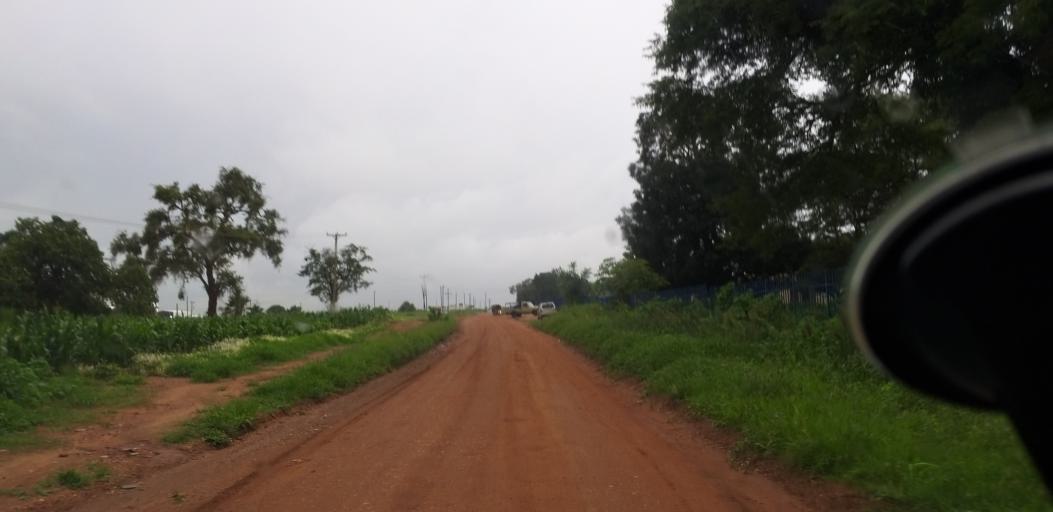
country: ZM
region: Lusaka
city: Lusaka
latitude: -15.5230
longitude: 28.2973
